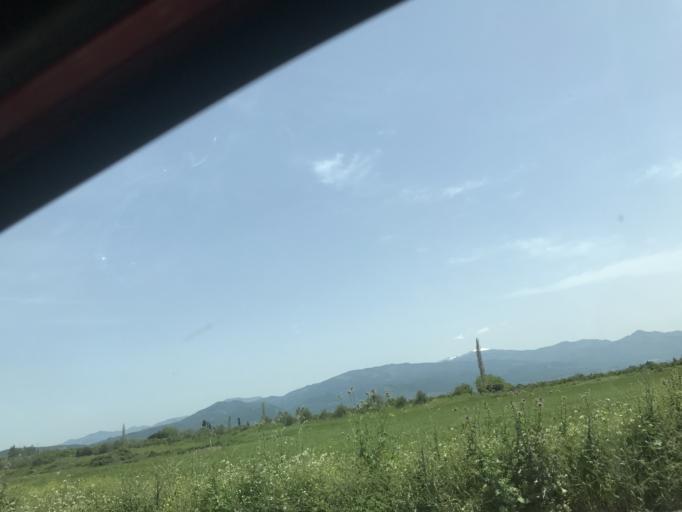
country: TR
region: Hatay
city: Mahmutlar
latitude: 36.9931
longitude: 36.1346
